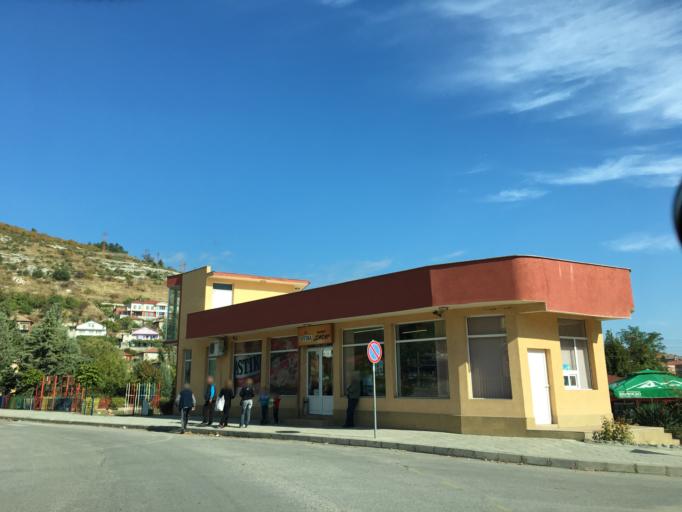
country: BG
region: Khaskovo
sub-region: Obshtina Ivaylovgrad
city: Ivaylovgrad
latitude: 41.5236
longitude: 26.1202
